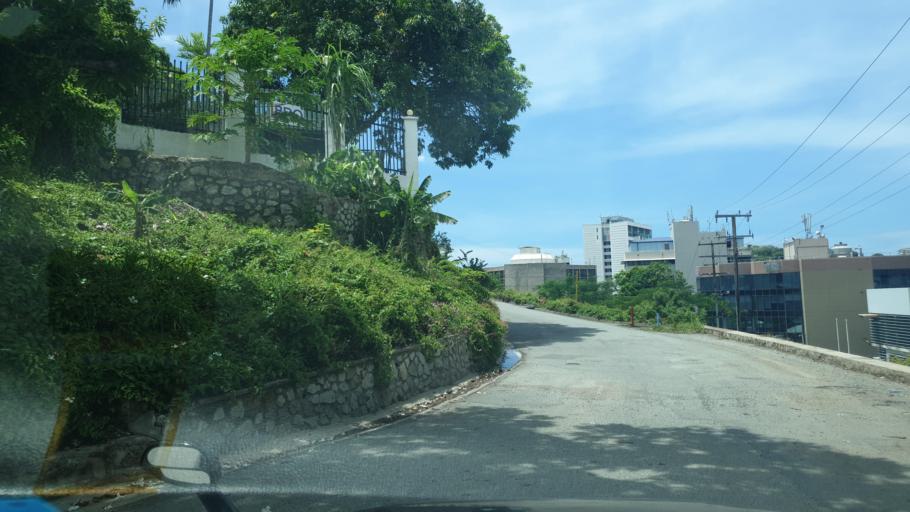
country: PG
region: National Capital
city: Port Moresby
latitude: -9.4769
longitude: 147.1530
